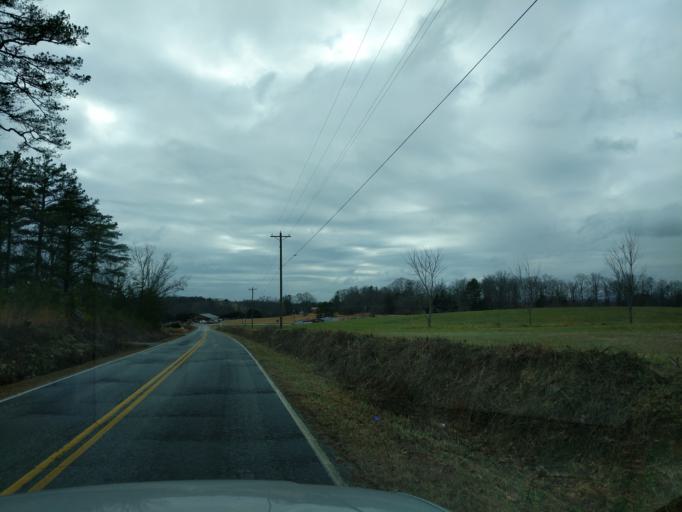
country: US
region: Georgia
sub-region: Rabun County
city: Clayton
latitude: 34.7787
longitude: -83.2574
